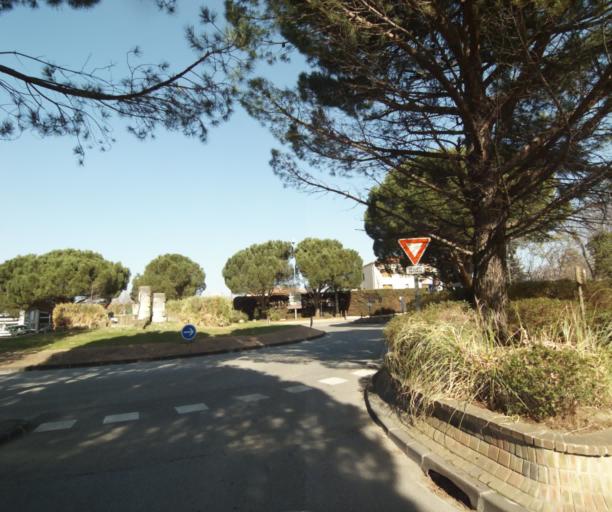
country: FR
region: Provence-Alpes-Cote d'Azur
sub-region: Departement des Bouches-du-Rhone
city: Gardanne
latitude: 43.4564
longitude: 5.4778
